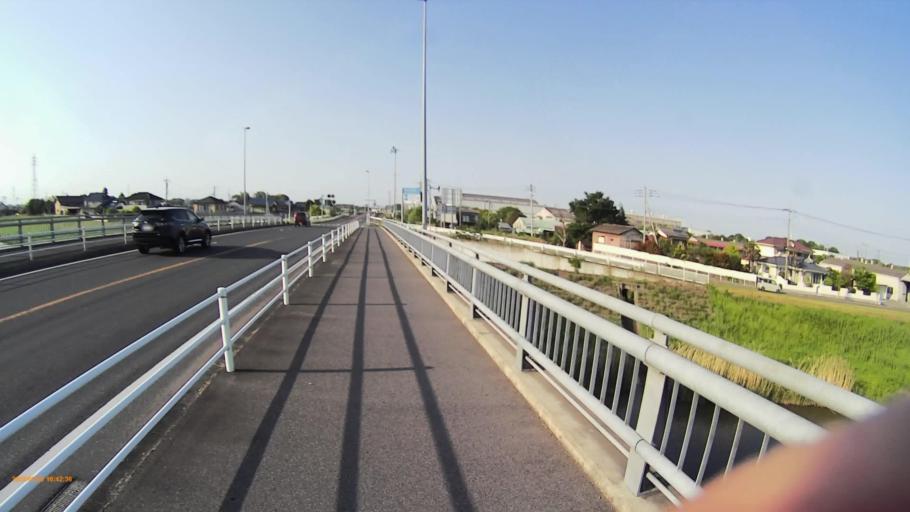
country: JP
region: Saitama
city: Satte
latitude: 36.0958
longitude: 139.7217
